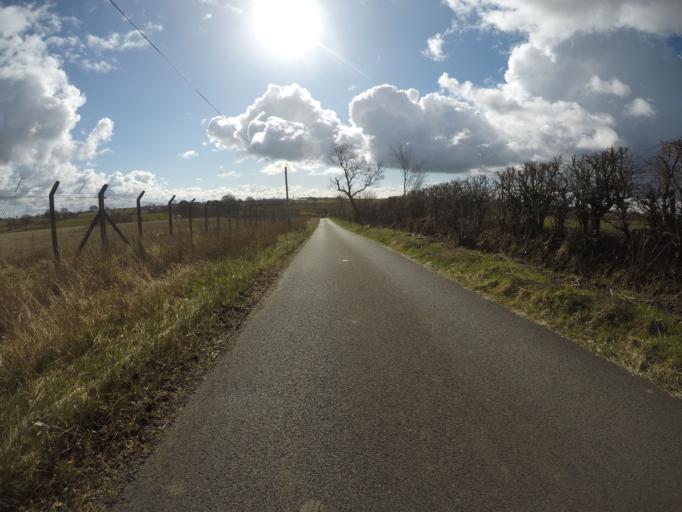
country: GB
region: Scotland
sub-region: North Ayrshire
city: Beith
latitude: 55.7173
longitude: -4.6273
